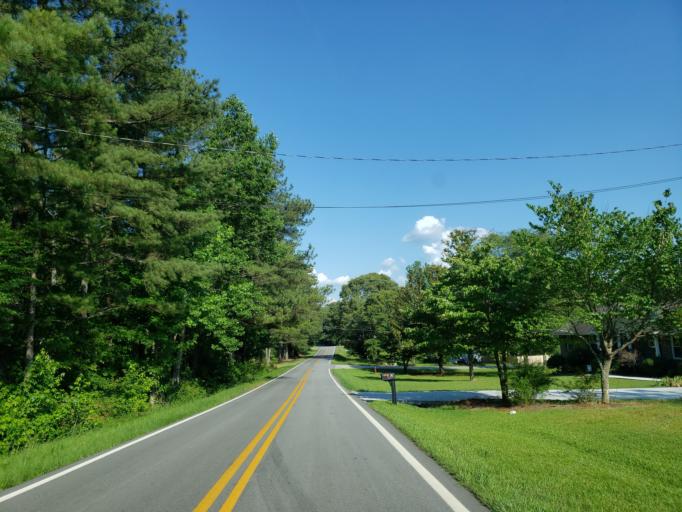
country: US
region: Georgia
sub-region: Haralson County
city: Bremen
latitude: 33.7073
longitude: -85.1138
